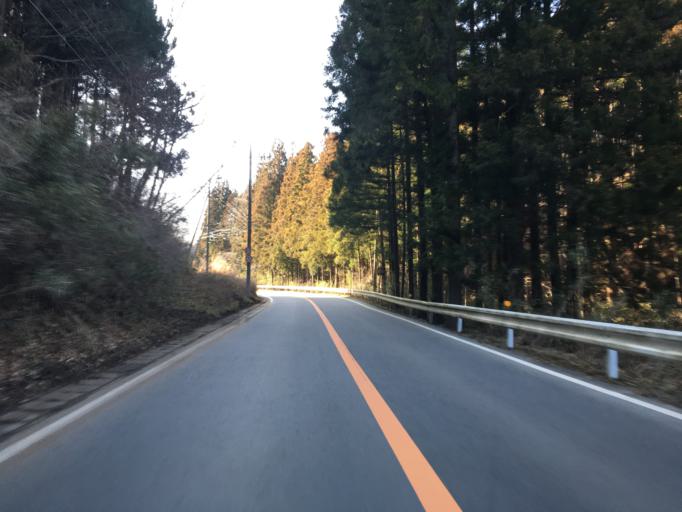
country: JP
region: Ibaraki
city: Takahagi
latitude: 36.7423
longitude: 140.5978
